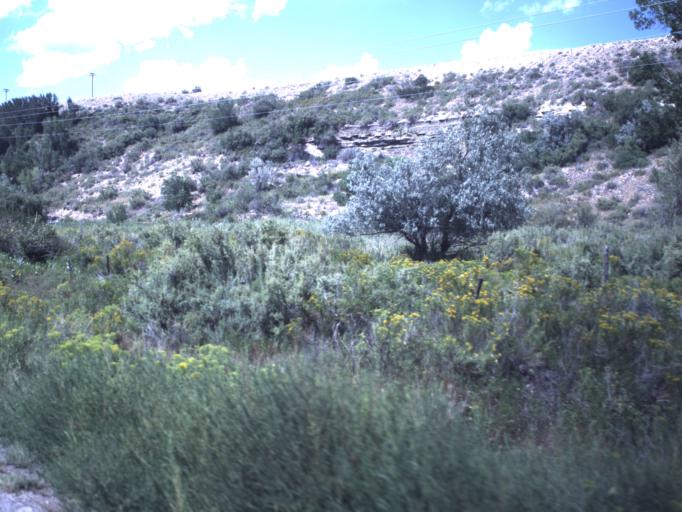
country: US
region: Utah
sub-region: Duchesne County
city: Duchesne
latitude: 40.1689
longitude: -110.4172
